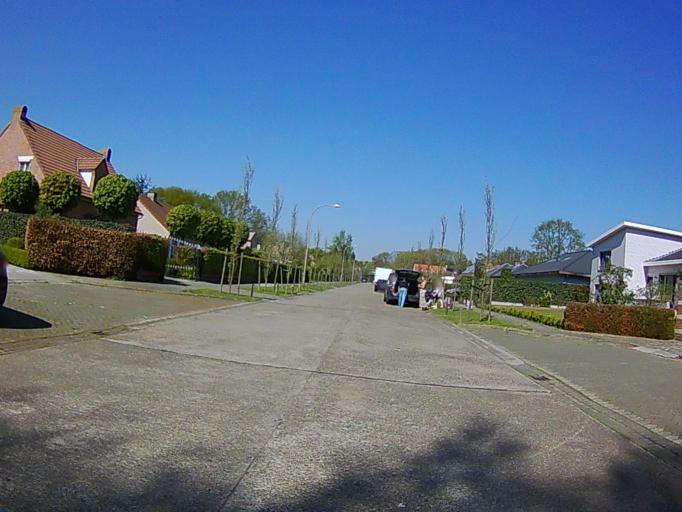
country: BE
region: Flanders
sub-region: Provincie Antwerpen
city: Brasschaat
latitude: 51.3079
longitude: 4.4972
